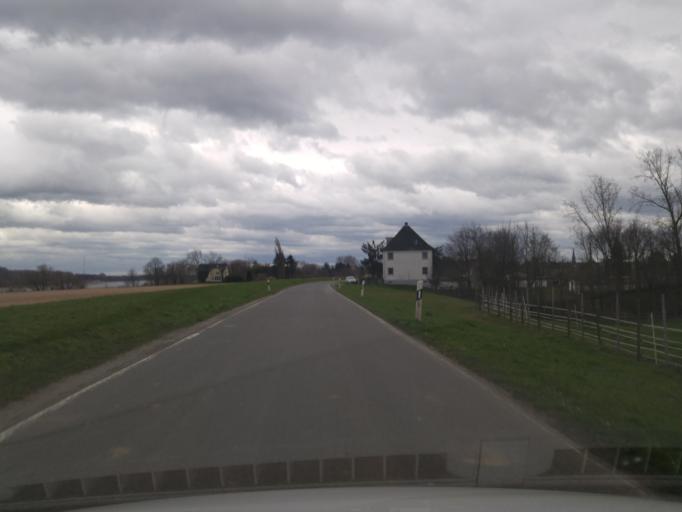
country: DE
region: North Rhine-Westphalia
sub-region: Regierungsbezirk Dusseldorf
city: Dormagen
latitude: 51.1327
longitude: 6.8432
